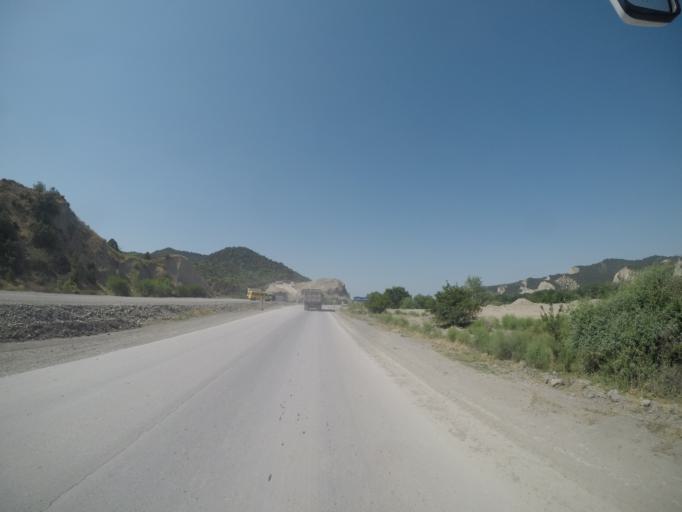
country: AZ
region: Agdas
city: Agdas
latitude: 40.7256
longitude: 47.5663
